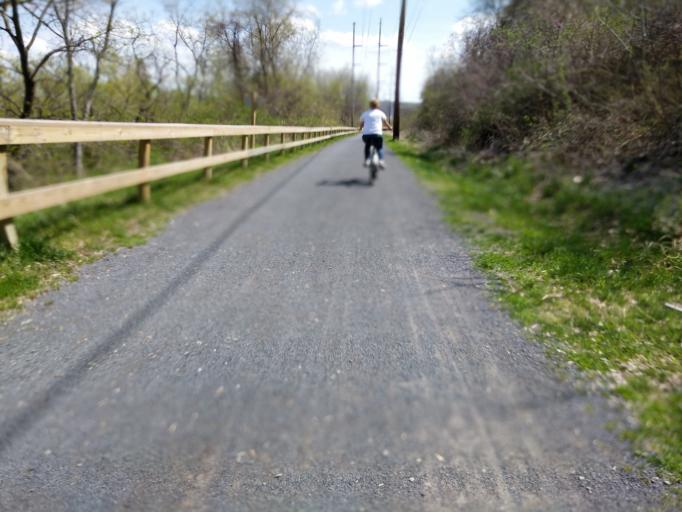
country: US
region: New York
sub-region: Tompkins County
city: Ithaca
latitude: 42.4515
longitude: -76.5166
